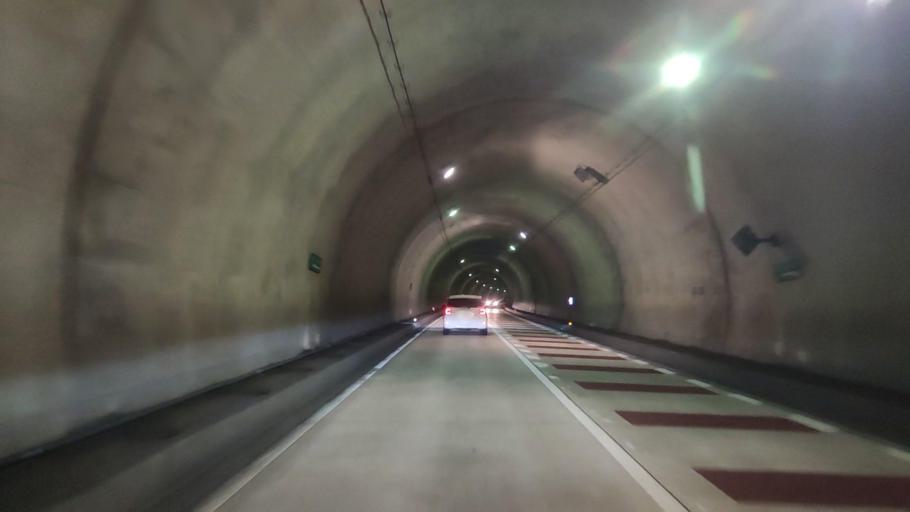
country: JP
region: Nara
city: Yoshino-cho
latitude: 34.2065
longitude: 135.9977
